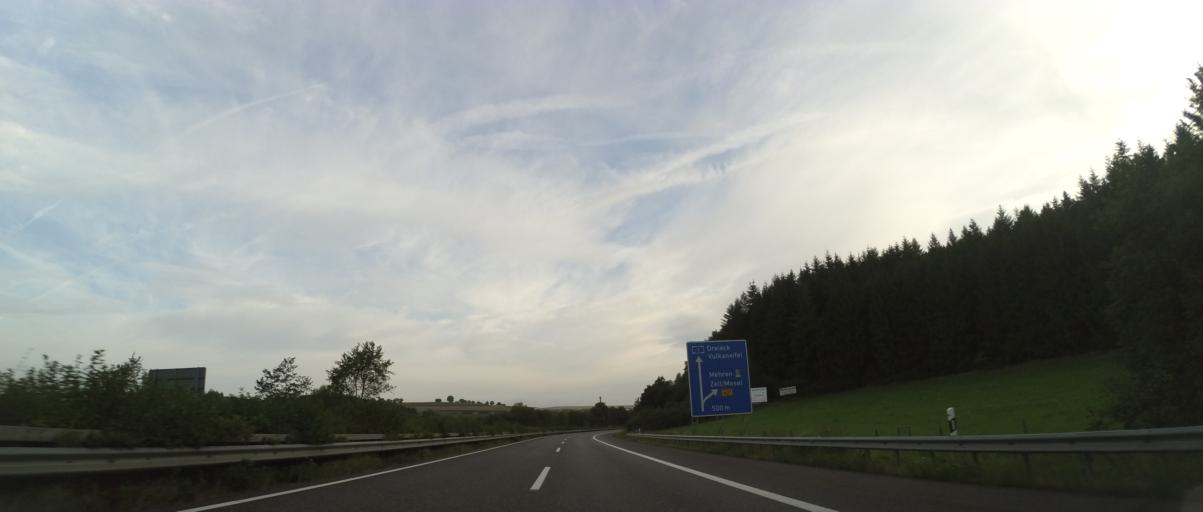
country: DE
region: Rheinland-Pfalz
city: Mehren
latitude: 50.1594
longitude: 6.8820
